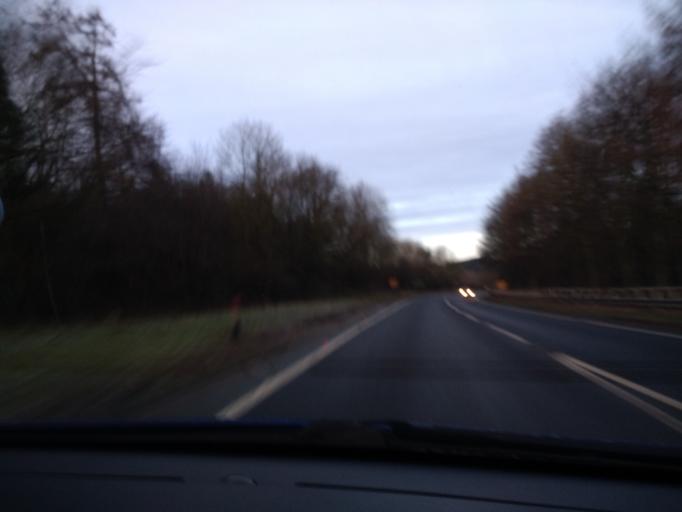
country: GB
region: England
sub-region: Northumberland
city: Warden
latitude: 54.9835
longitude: -2.1489
